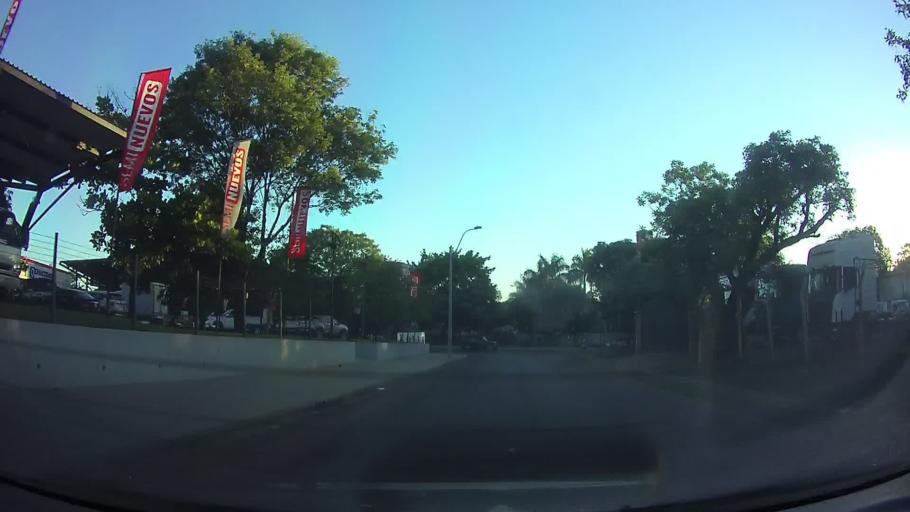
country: PY
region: Central
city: Fernando de la Mora
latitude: -25.3060
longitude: -57.5547
